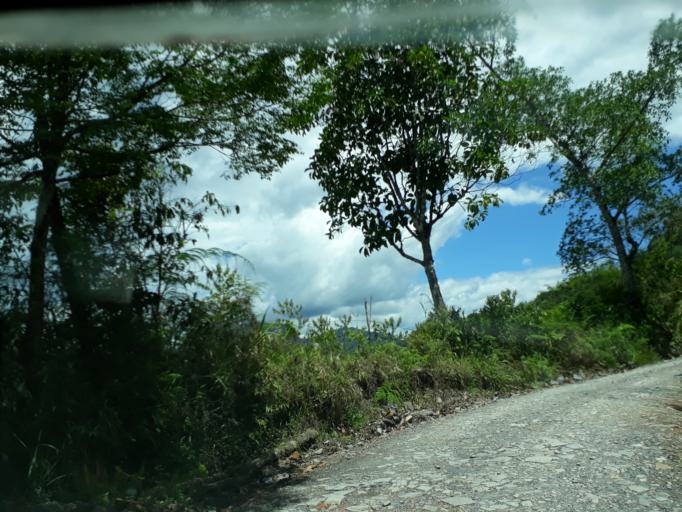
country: CO
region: Cundinamarca
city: Topaipi
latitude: 5.3662
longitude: -74.1965
